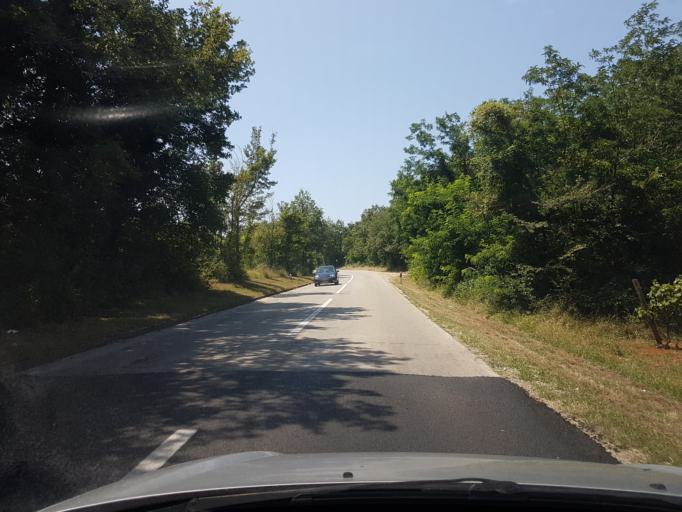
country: HR
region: Istarska
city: Vrsar
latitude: 45.1619
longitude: 13.6854
